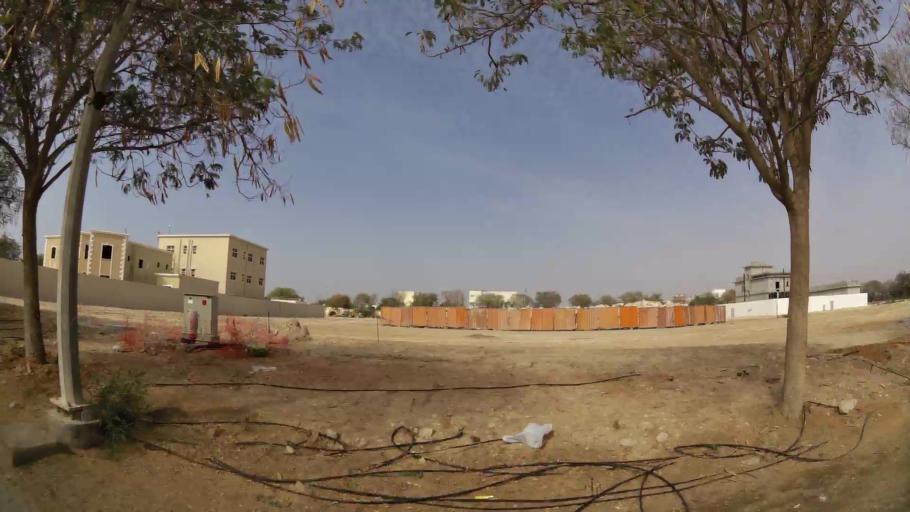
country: AE
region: Abu Dhabi
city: Abu Dhabi
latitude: 24.5999
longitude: 54.7021
